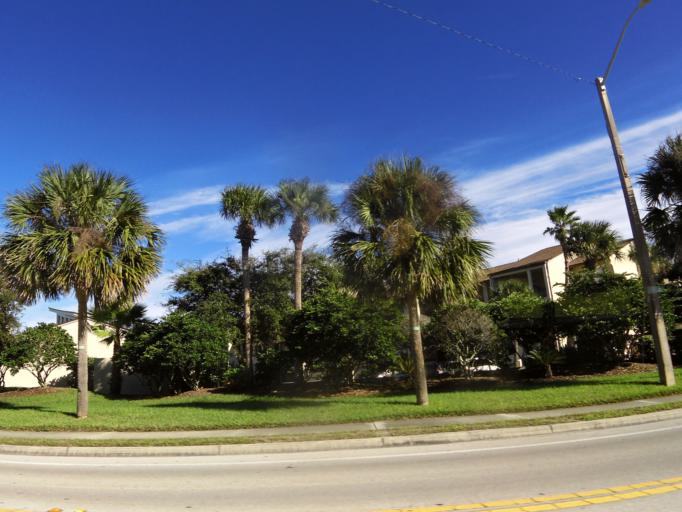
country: US
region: Florida
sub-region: Saint Johns County
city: Saint Augustine Beach
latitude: 29.8379
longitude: -81.2676
